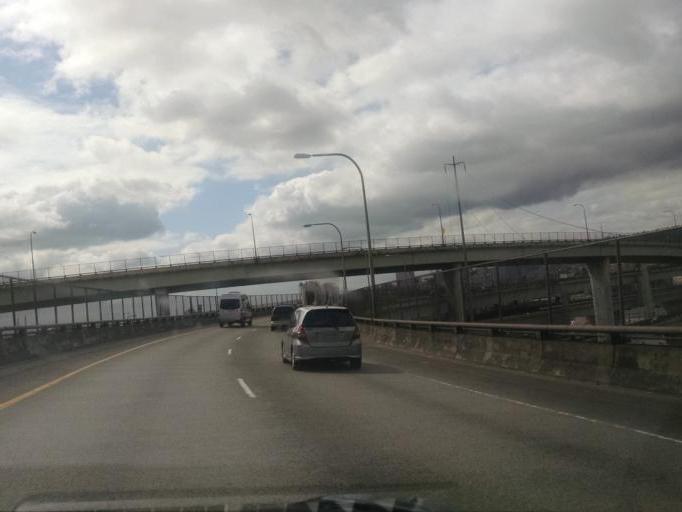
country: US
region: Oregon
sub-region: Multnomah County
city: Portland
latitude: 45.5446
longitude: -122.6769
